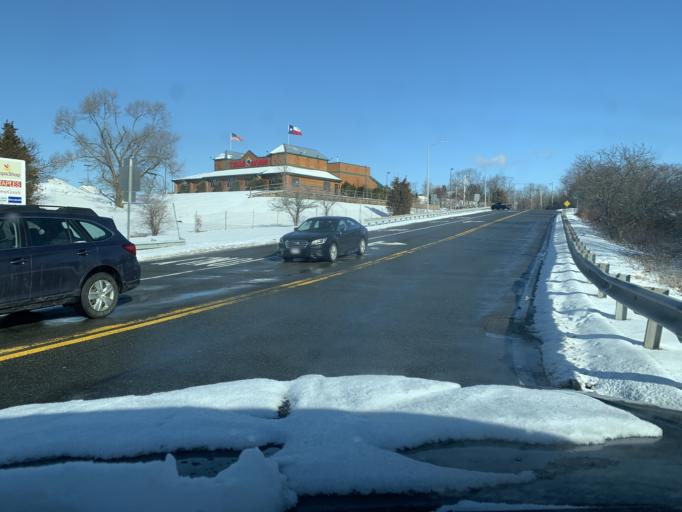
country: US
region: Massachusetts
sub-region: Essex County
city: Danvers
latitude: 42.5828
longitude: -70.9648
